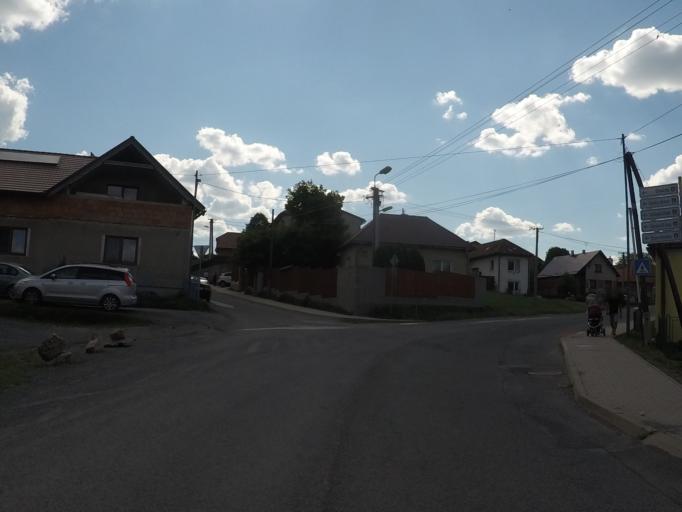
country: SK
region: Presovsky
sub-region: Okres Poprad
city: Poprad
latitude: 48.9942
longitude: 20.3567
